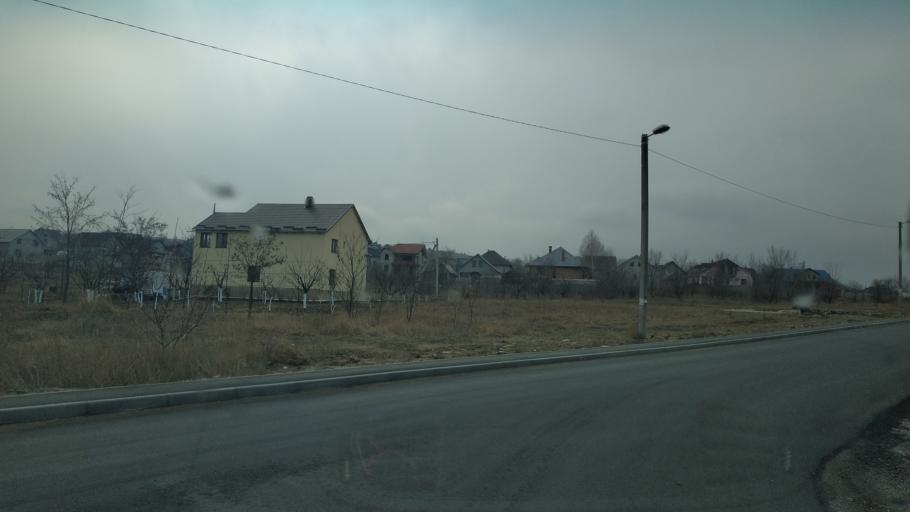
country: MD
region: Chisinau
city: Singera
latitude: 46.9139
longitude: 28.9906
